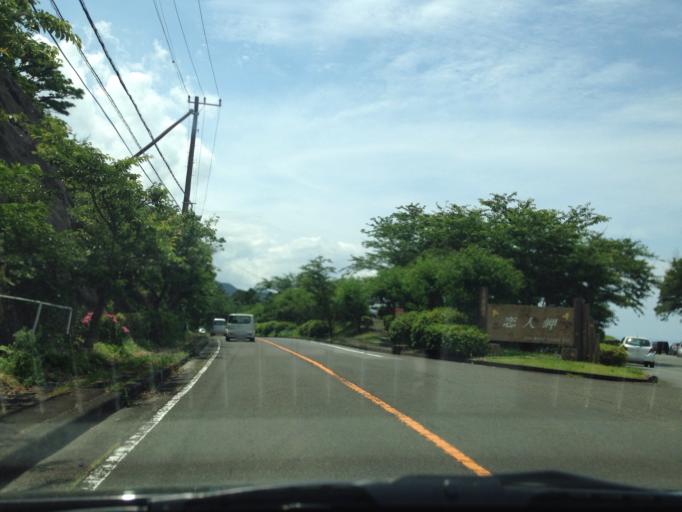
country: JP
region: Shizuoka
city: Heda
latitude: 34.8682
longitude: 138.7614
